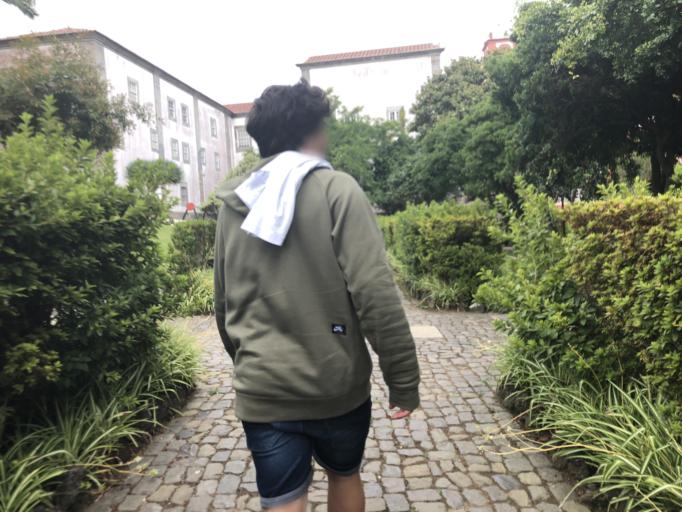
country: PT
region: Azores
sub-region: Angra do Heroismo
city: Angra do Heroismo
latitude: 38.6571
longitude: -27.2179
